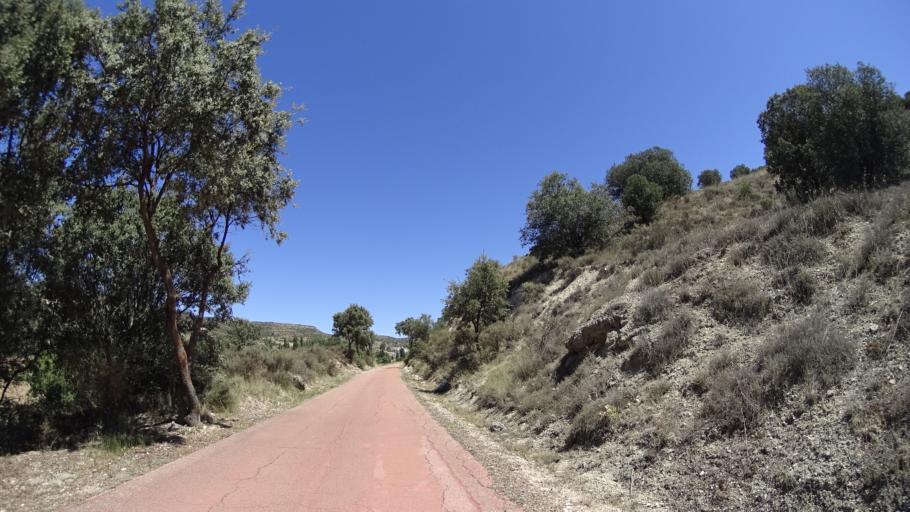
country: ES
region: Madrid
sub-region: Provincia de Madrid
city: Ambite
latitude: 40.3159
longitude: -3.1885
